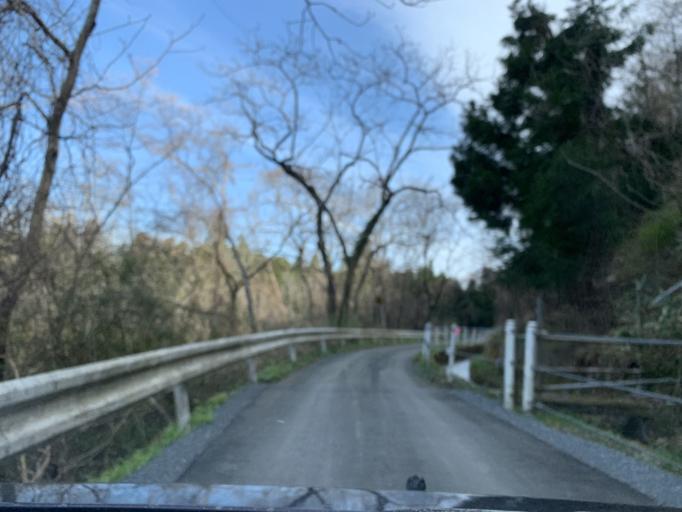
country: JP
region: Iwate
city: Ichinoseki
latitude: 38.9354
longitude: 141.0707
